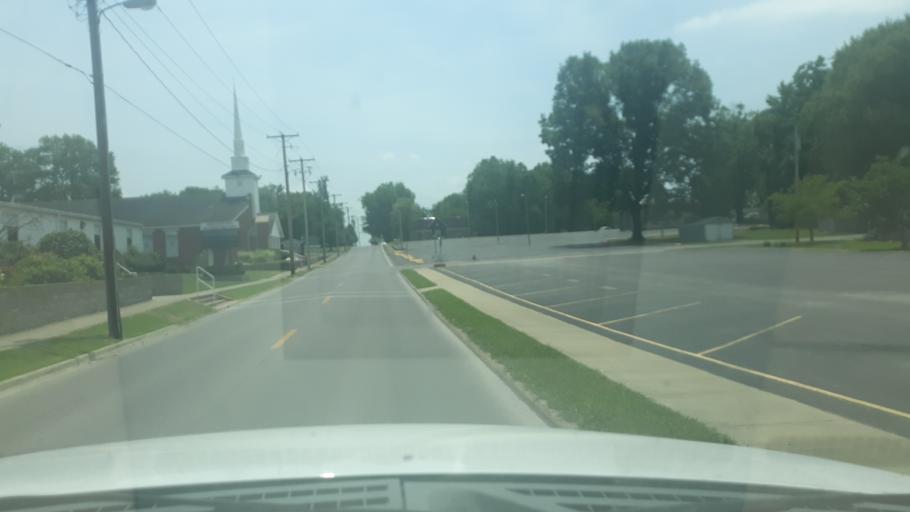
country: US
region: Illinois
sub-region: Saline County
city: Harrisburg
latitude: 37.7235
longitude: -88.5531
